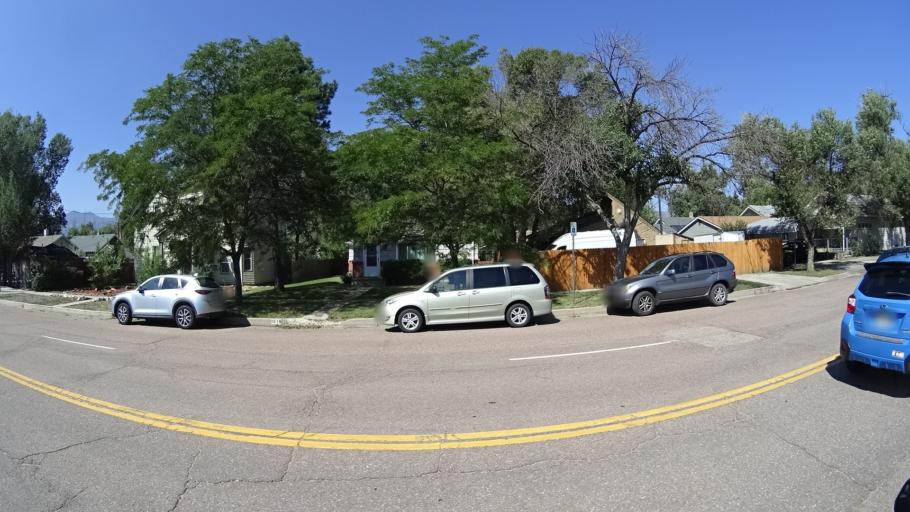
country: US
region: Colorado
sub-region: El Paso County
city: Colorado Springs
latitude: 38.8611
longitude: -104.8184
